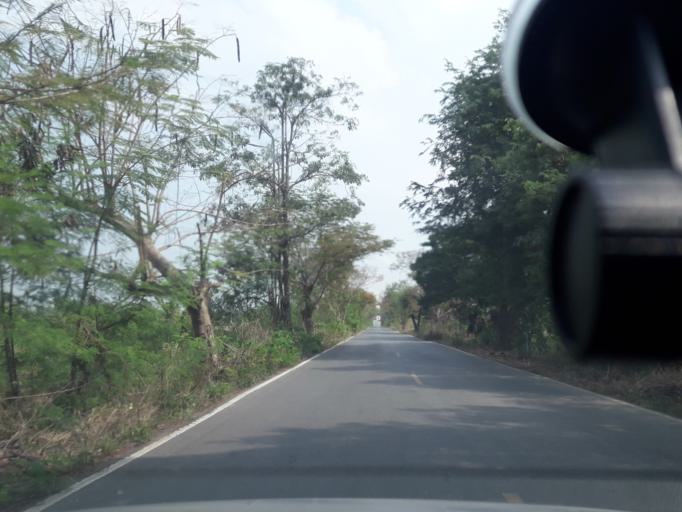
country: TH
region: Pathum Thani
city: Nong Suea
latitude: 14.1967
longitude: 100.8854
